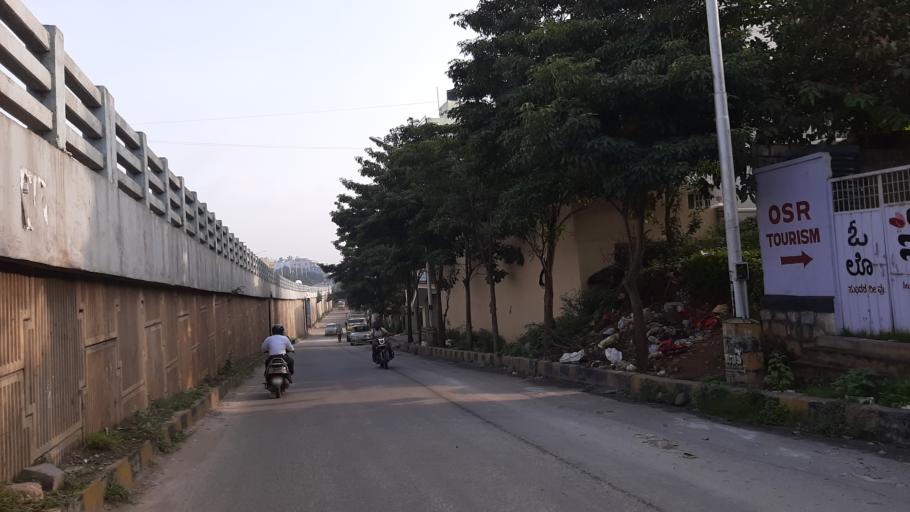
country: IN
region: Karnataka
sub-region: Bangalore Urban
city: Bangalore
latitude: 12.9735
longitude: 77.5133
